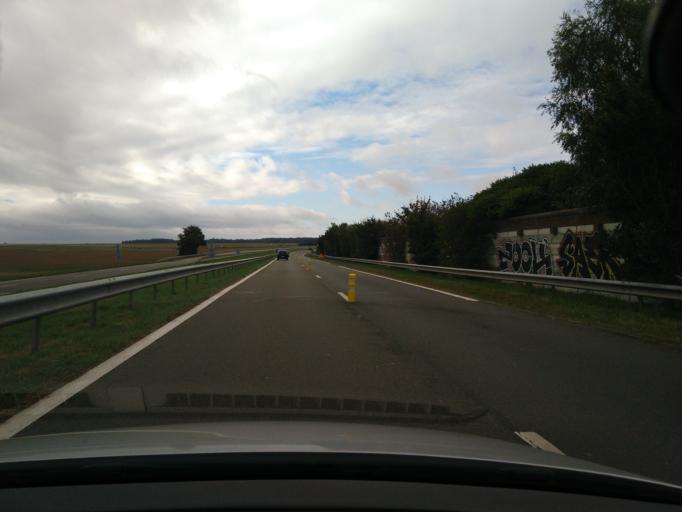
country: FR
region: Ile-de-France
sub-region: Departement des Yvelines
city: Houdan
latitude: 48.7768
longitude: 1.5622
